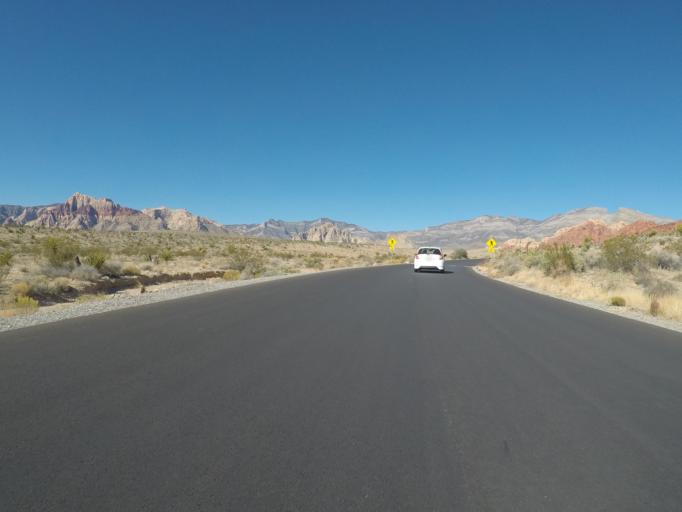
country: US
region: Nevada
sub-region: Clark County
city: Summerlin South
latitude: 36.1383
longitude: -115.4265
